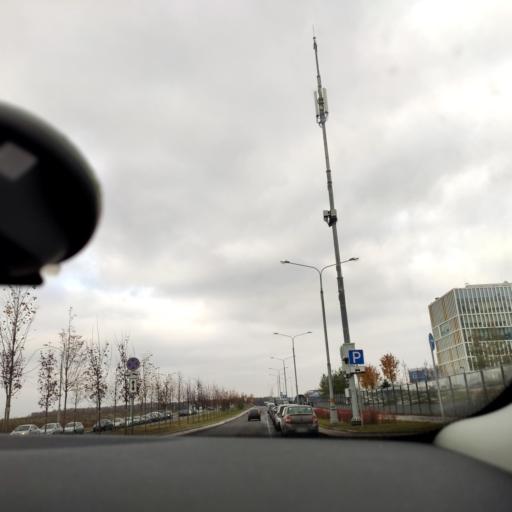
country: RU
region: Moskovskaya
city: Kommunarka
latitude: 55.5670
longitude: 37.4637
